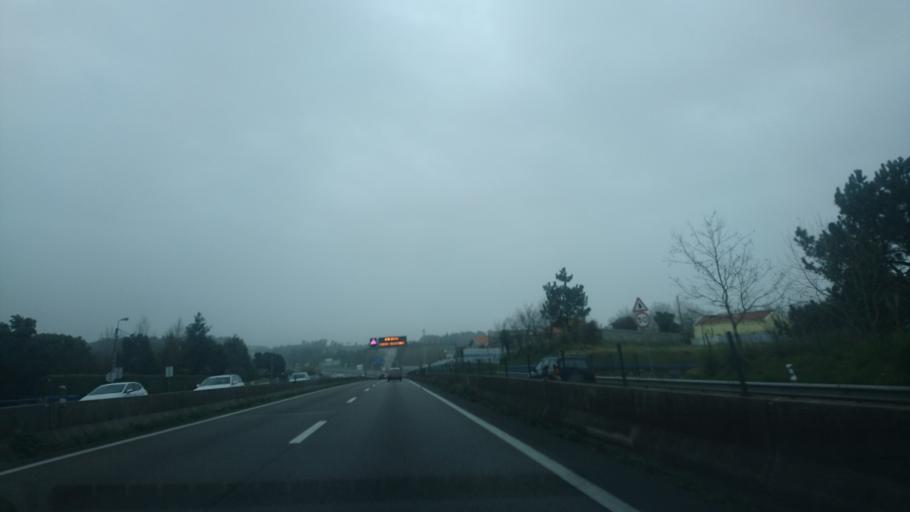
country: PT
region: Porto
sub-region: Vila Nova de Gaia
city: Vilar do Paraiso
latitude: 41.0935
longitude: -8.6296
